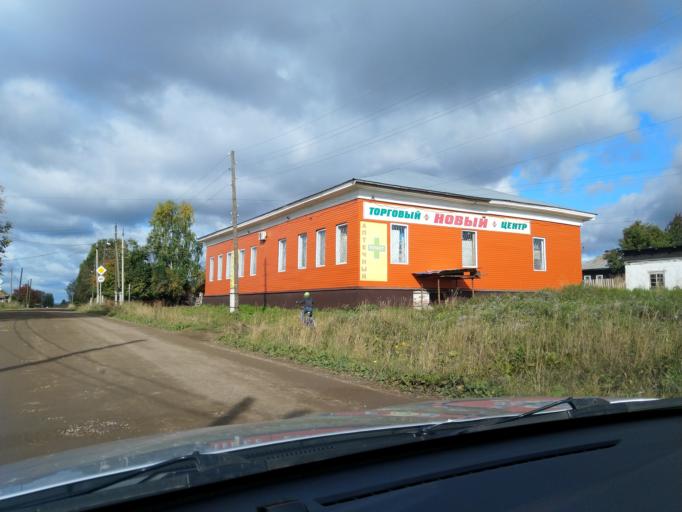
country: RU
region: Perm
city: Pozhva
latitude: 59.0880
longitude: 56.0774
